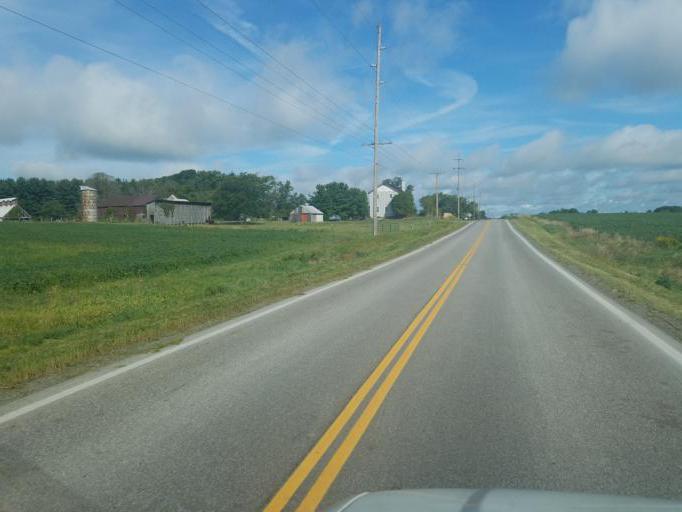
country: US
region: Ohio
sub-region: Wayne County
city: West Salem
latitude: 40.9993
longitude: -82.1132
